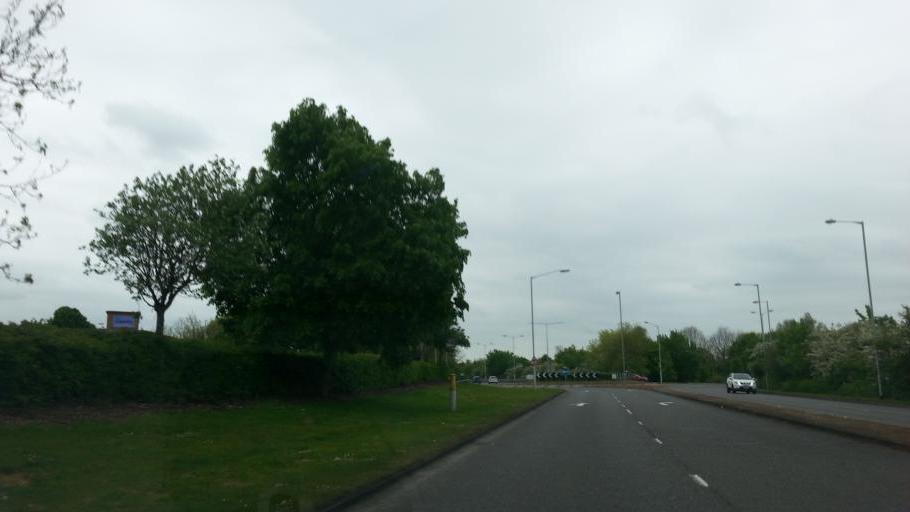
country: GB
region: England
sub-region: Peterborough
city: Marholm
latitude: 52.6075
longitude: -0.2737
